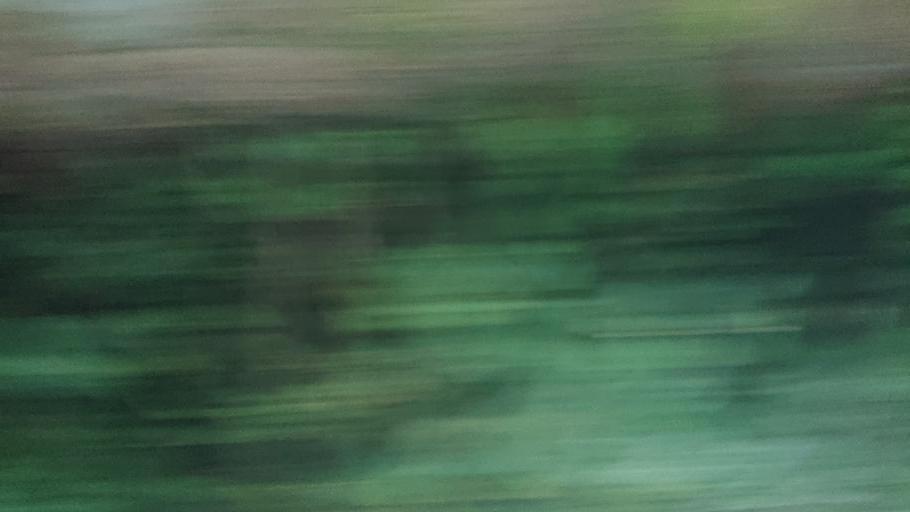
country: TW
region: Taiwan
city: Lugu
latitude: 23.5256
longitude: 120.7099
